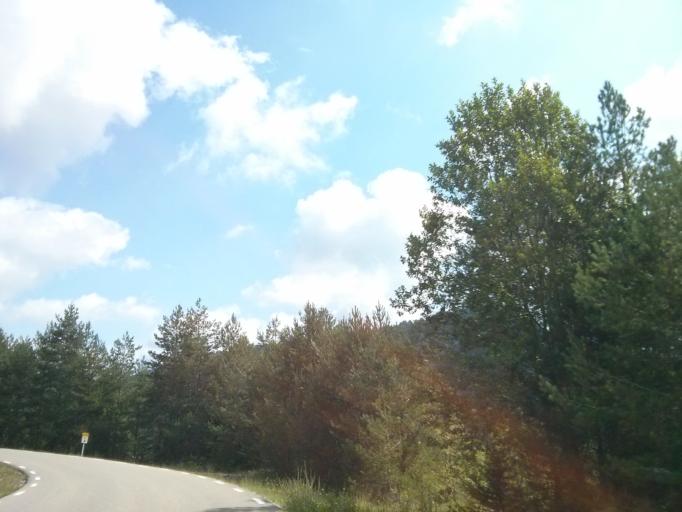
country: ES
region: Catalonia
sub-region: Provincia de Barcelona
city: Borreda
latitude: 42.1565
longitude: 2.0031
